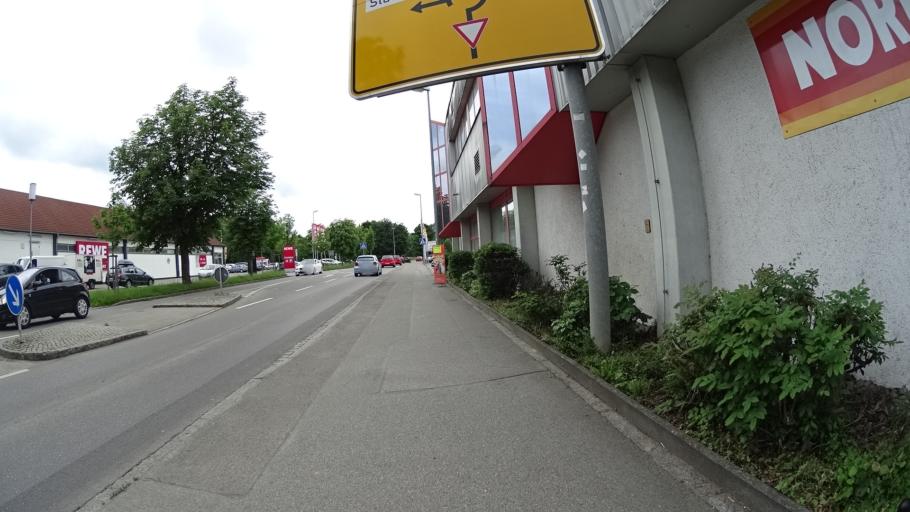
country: DE
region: Bavaria
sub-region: Swabia
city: Weissenhorn
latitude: 48.3027
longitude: 10.1526
